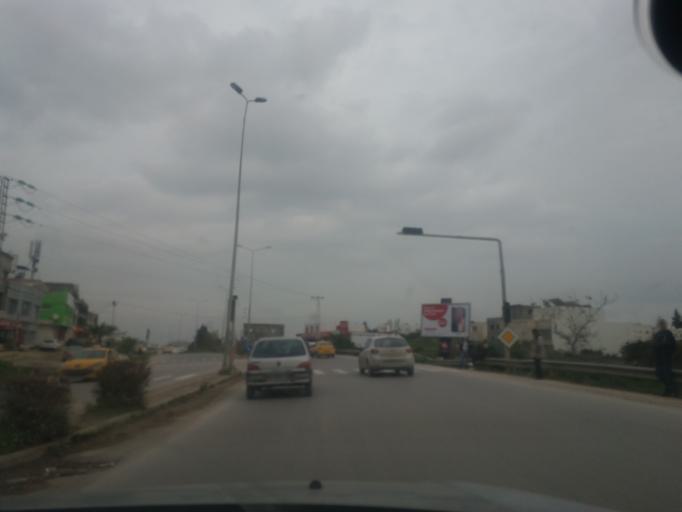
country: TN
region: Tunis
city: Tunis
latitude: 36.8533
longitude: 10.1378
